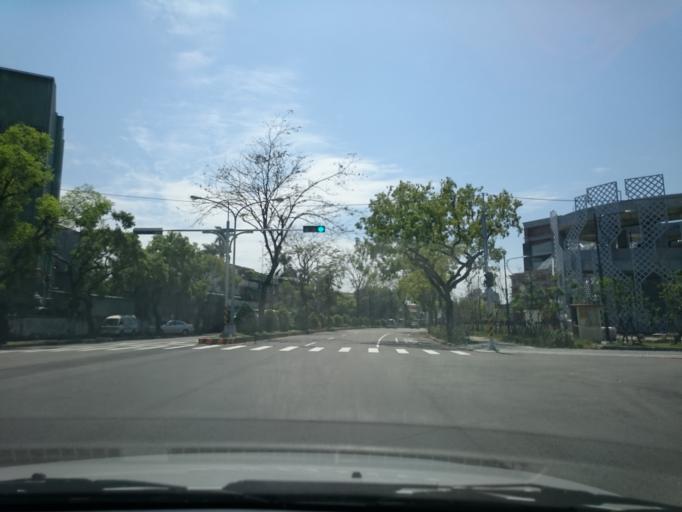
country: TW
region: Taiwan
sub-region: Taichung City
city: Taichung
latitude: 24.1350
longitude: 120.6960
